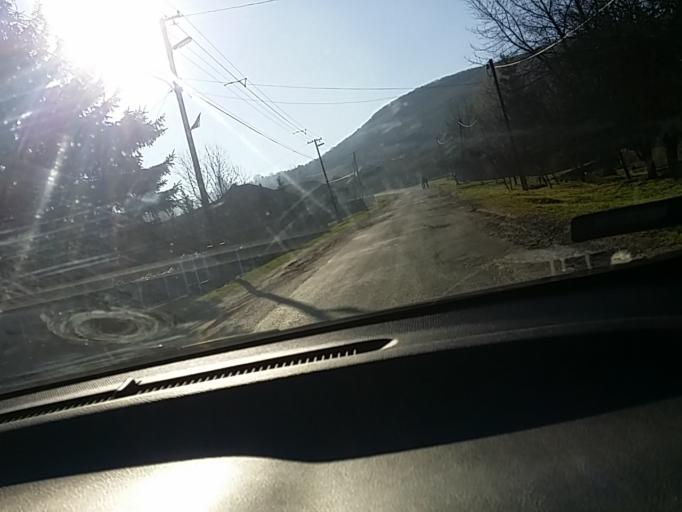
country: HU
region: Heves
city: Szilvasvarad
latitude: 48.1561
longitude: 20.4951
